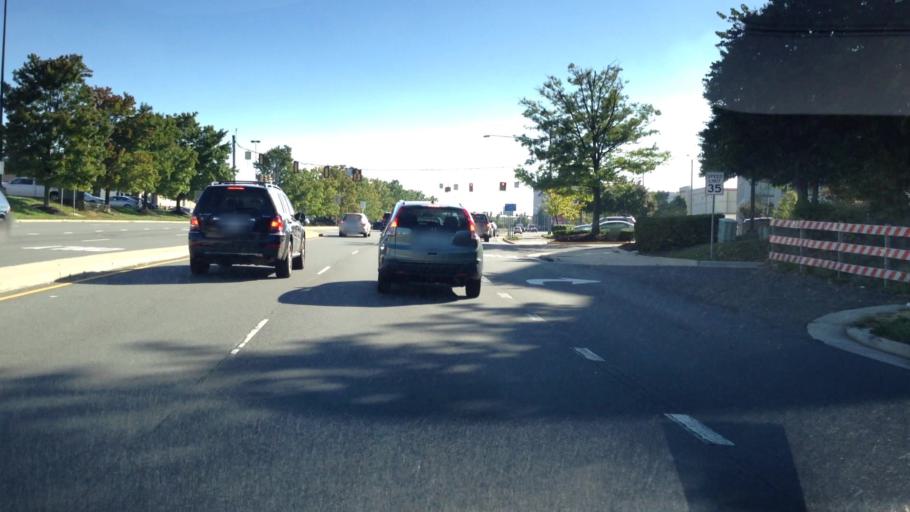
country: US
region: Virginia
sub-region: City of Fairfax
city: Fairfax
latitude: 38.8567
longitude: -77.3360
